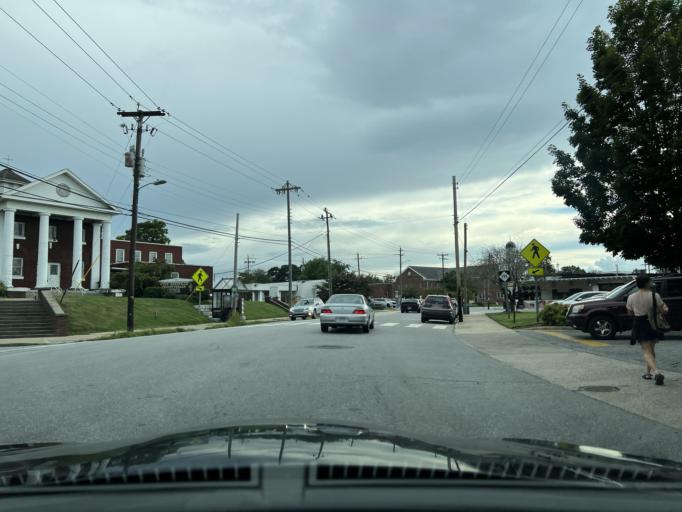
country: US
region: North Carolina
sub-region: Buncombe County
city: Asheville
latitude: 35.5778
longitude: -82.5907
